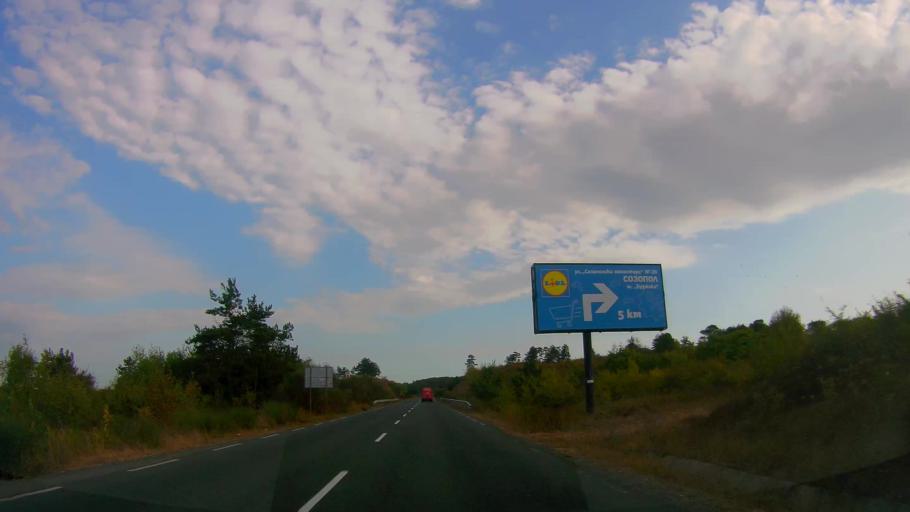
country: BG
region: Burgas
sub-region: Obshtina Sozopol
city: Sozopol
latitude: 42.3990
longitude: 27.6754
